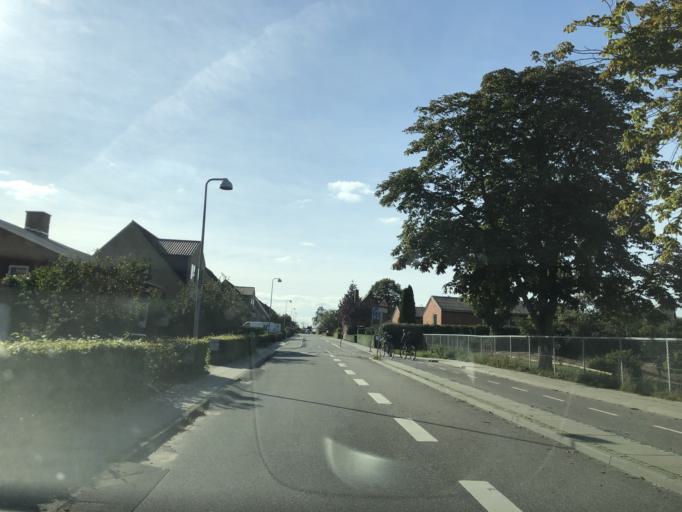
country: DK
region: Central Jutland
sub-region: Syddjurs Kommune
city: Hornslet
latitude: 56.3142
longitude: 10.3149
